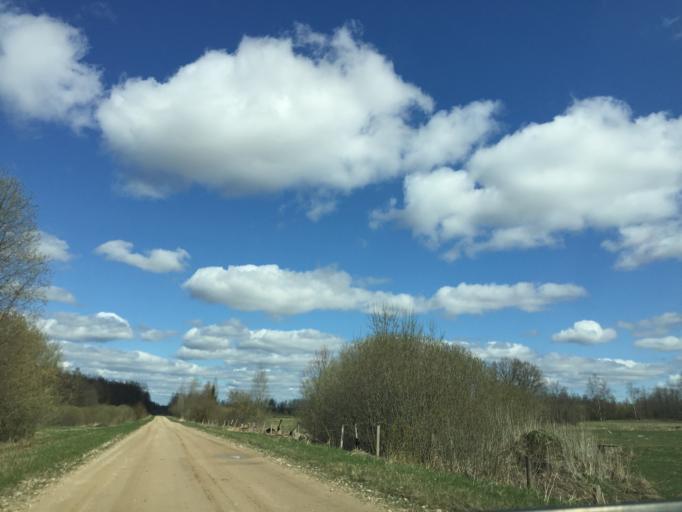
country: LV
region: Vilanu
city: Vilani
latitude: 56.6753
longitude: 27.0934
